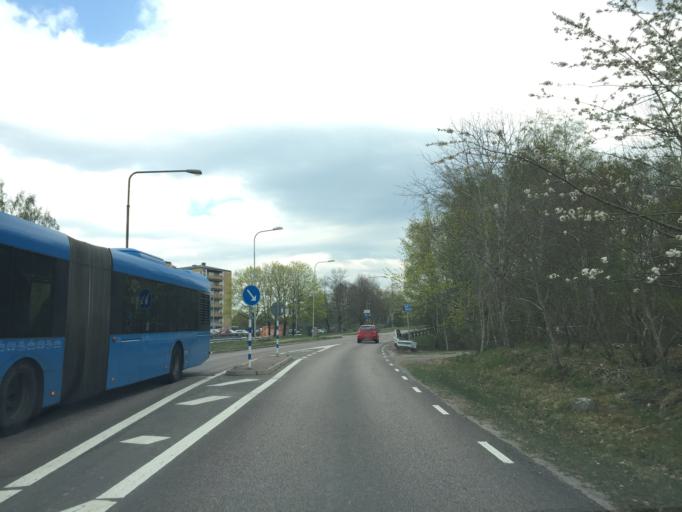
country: SE
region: Vaestra Goetaland
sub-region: Goteborg
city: Rannebergen
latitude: 57.7998
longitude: 12.0738
